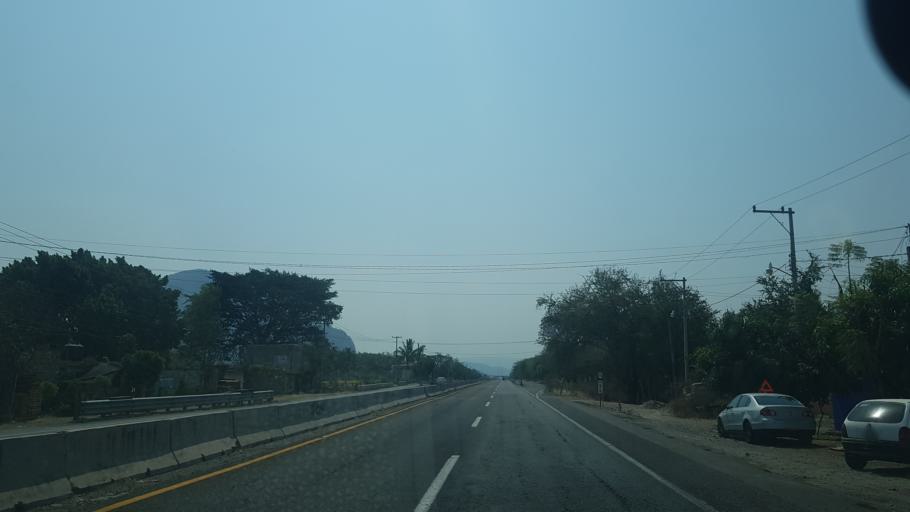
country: MX
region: Morelos
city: Jantetelco
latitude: 18.7116
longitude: -98.7822
